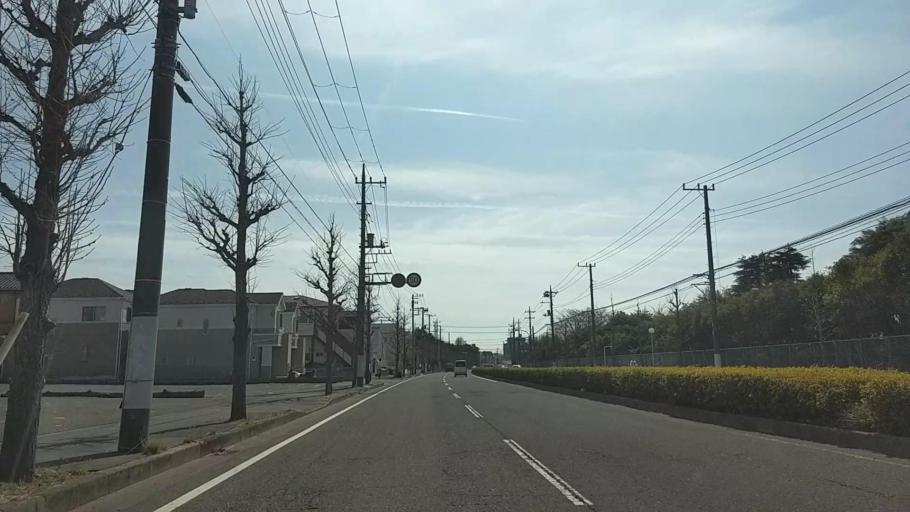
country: JP
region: Kanagawa
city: Fujisawa
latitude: 35.3872
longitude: 139.4573
